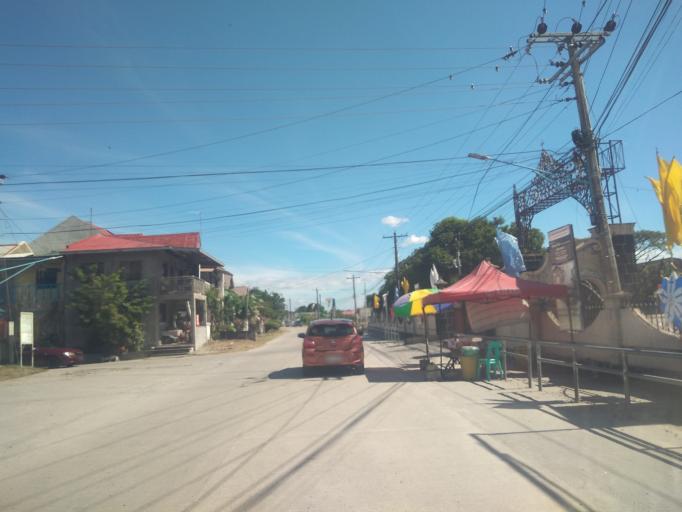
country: PH
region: Central Luzon
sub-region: Province of Pampanga
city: Bacolor
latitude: 15.0010
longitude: 120.6487
